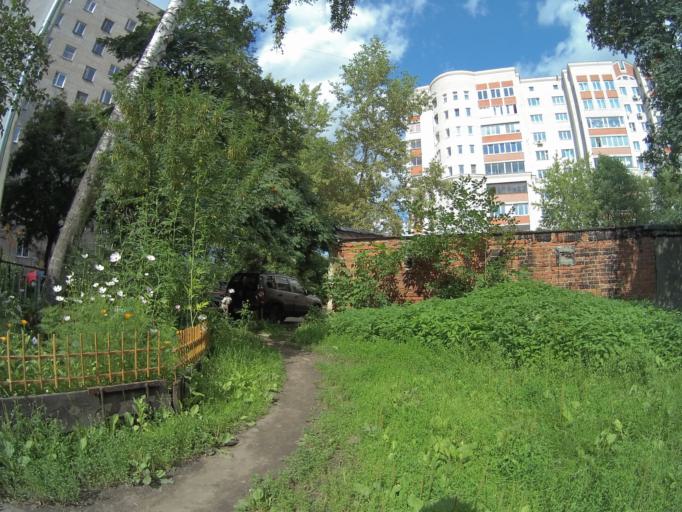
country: RU
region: Vladimir
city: Vladimir
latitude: 56.1427
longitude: 40.4004
